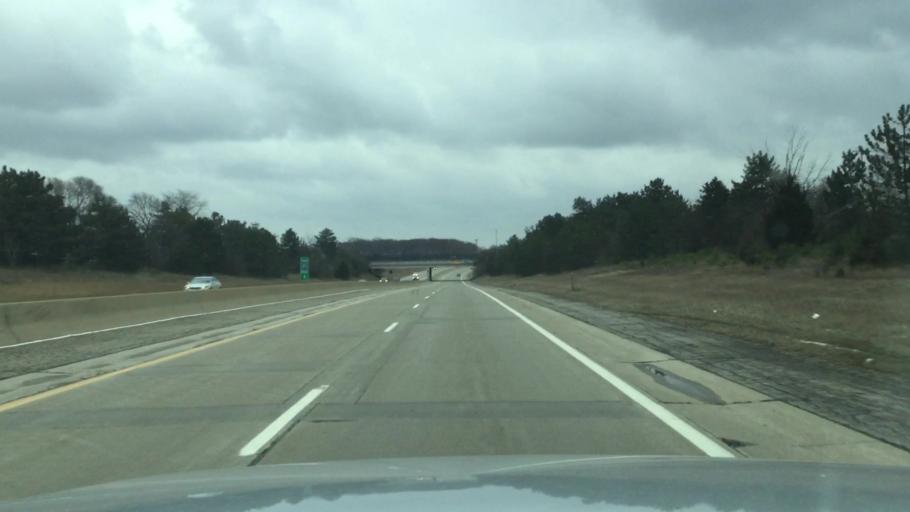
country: US
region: Michigan
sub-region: Genesee County
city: Flint
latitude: 42.9553
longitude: -83.6826
